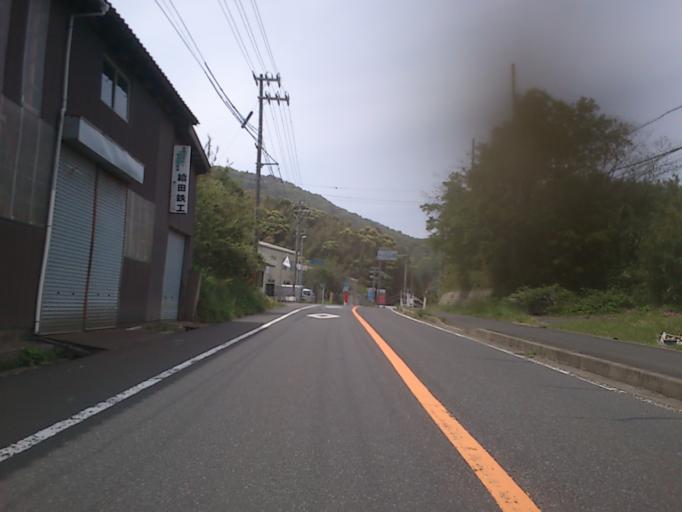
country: JP
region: Kyoto
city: Miyazu
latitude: 35.7216
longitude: 135.1030
